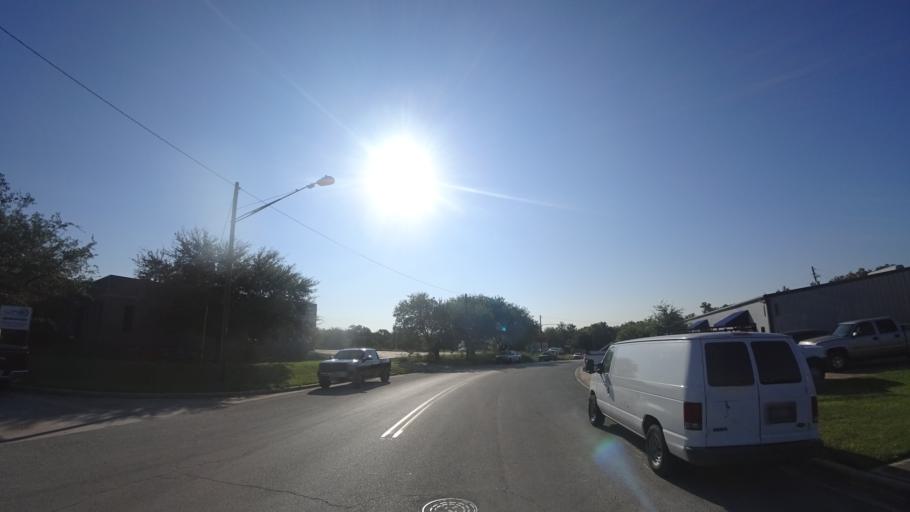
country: US
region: Texas
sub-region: Travis County
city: Manor
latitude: 30.3232
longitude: -97.6542
